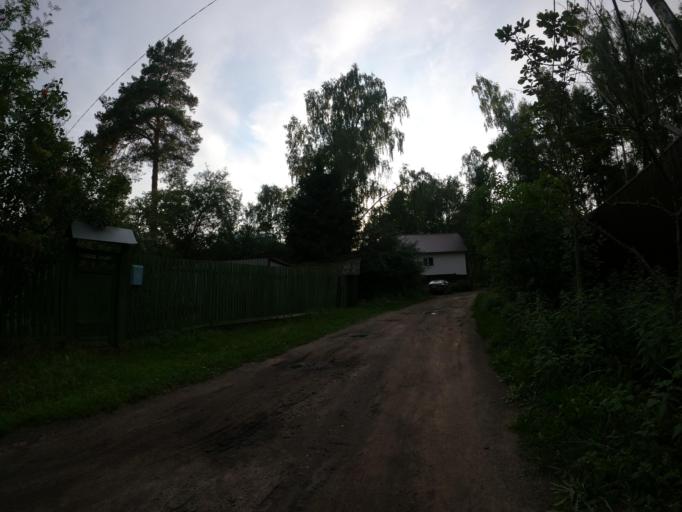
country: RU
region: Moskovskaya
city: Bykovo
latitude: 55.6371
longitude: 38.0847
